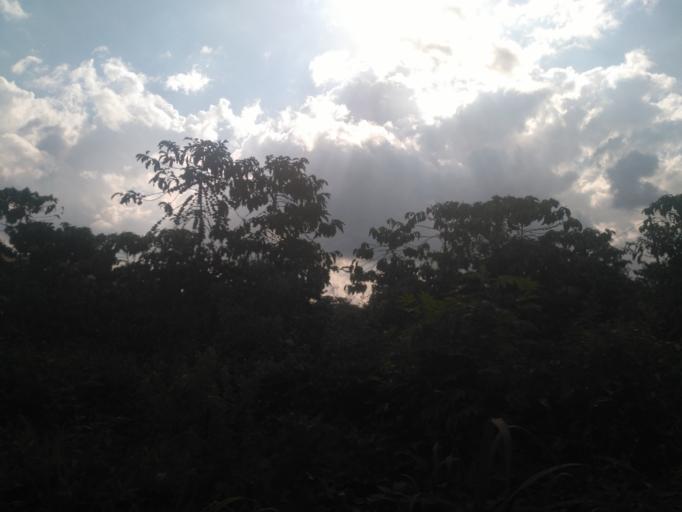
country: UG
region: Central Region
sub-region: Wakiso District
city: Kajansi
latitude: 0.2668
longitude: 32.4369
